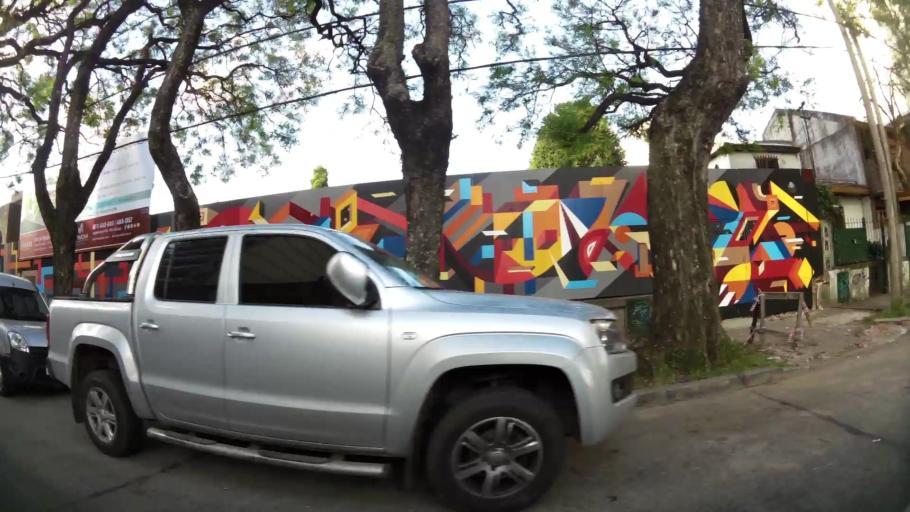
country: AR
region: Buenos Aires
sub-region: Partido de General San Martin
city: General San Martin
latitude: -34.5477
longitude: -58.5582
